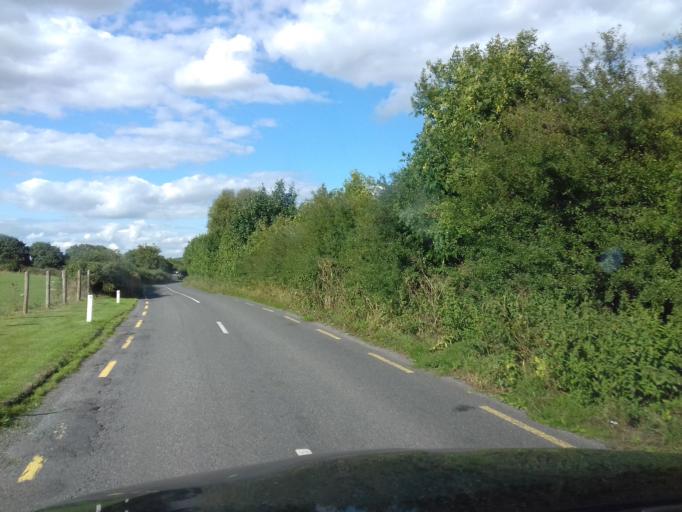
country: IE
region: Leinster
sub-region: Kilkenny
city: Thomastown
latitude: 52.5446
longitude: -7.0845
